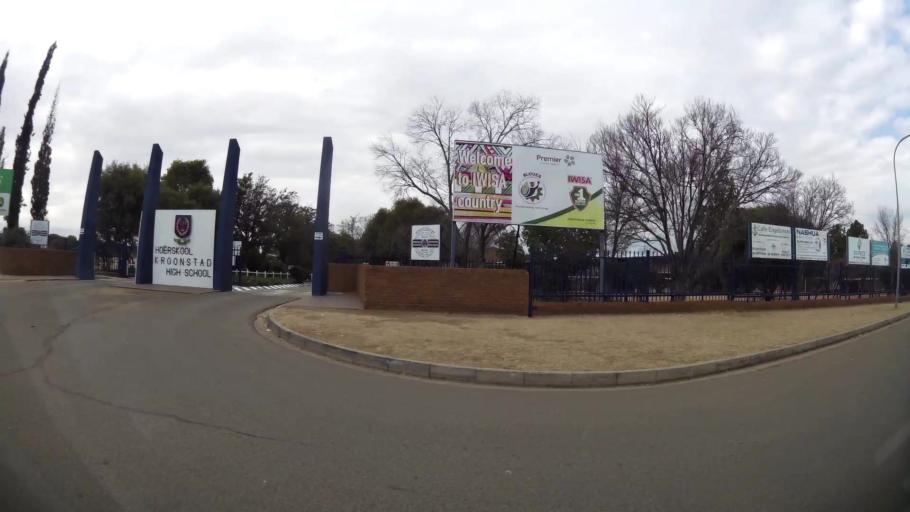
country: ZA
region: Orange Free State
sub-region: Fezile Dabi District Municipality
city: Kroonstad
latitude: -27.6360
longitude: 27.2338
